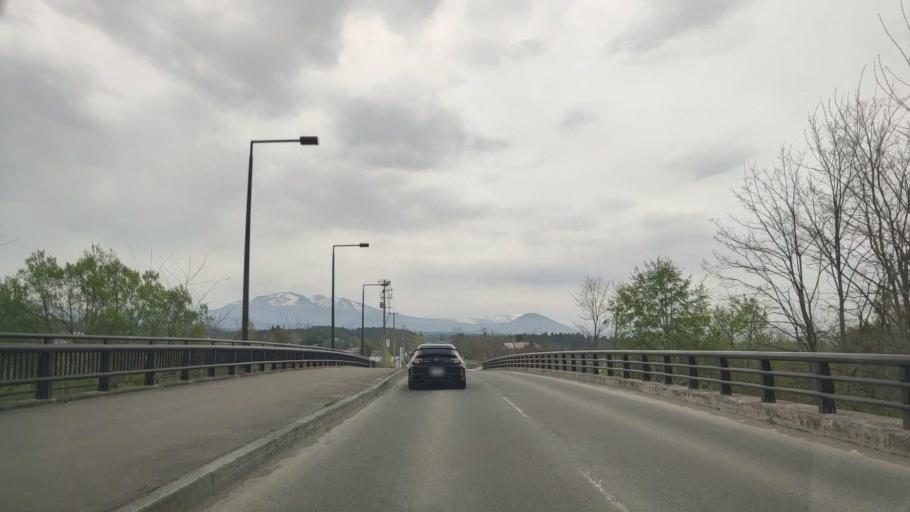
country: JP
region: Aomori
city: Aomori Shi
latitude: 40.7974
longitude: 140.7842
